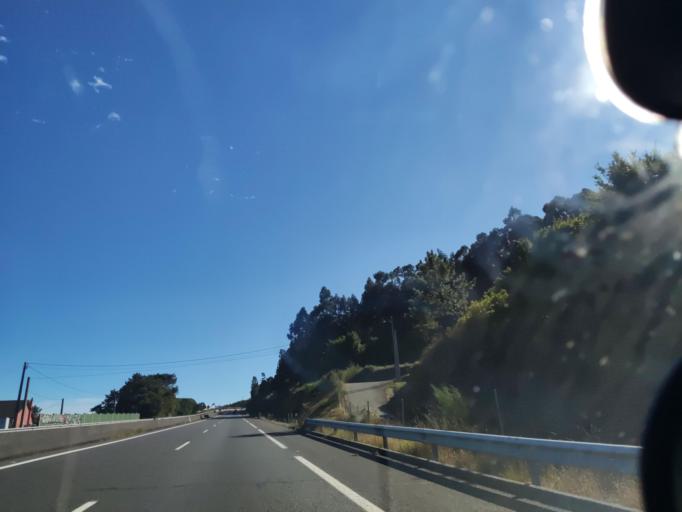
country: ES
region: Galicia
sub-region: Provincia da Coruna
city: Boiro
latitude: 42.6527
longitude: -8.9014
